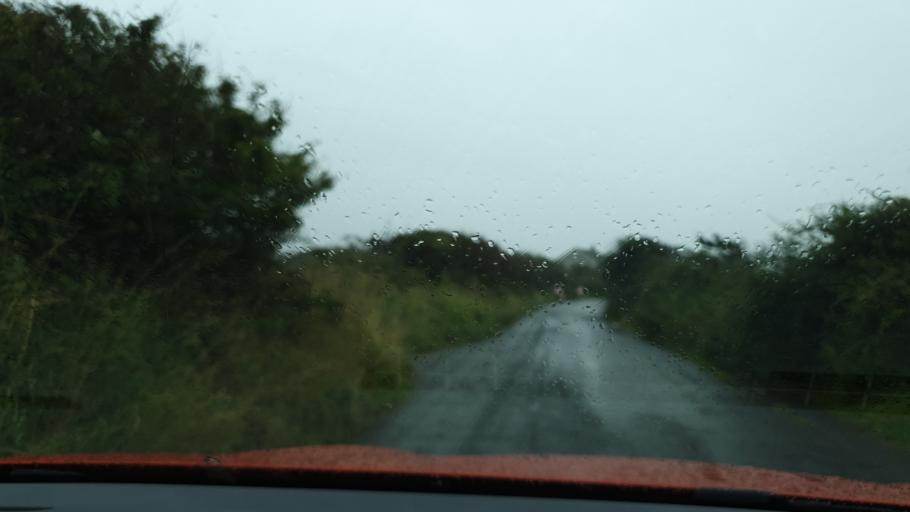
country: GB
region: England
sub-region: Cumbria
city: Barrow in Furness
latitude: 54.1220
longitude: -3.2585
